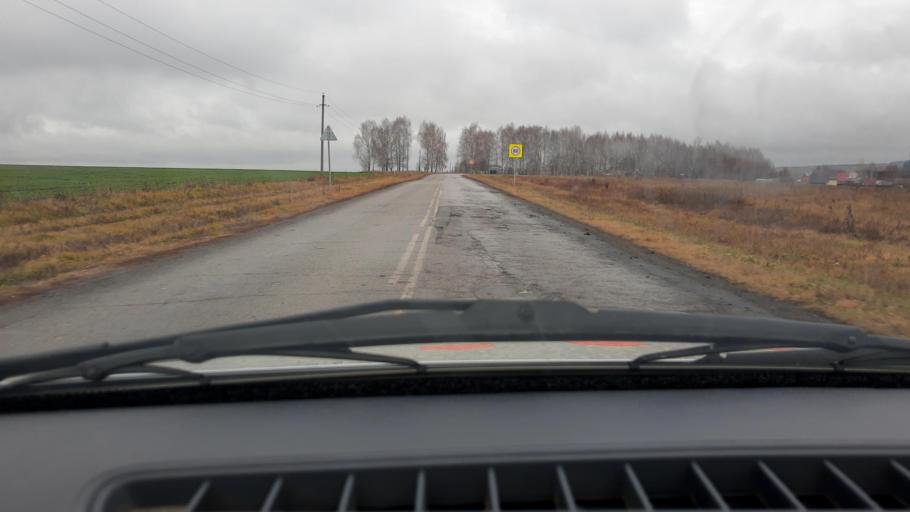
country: RU
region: Bashkortostan
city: Iglino
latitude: 54.7665
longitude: 56.3801
